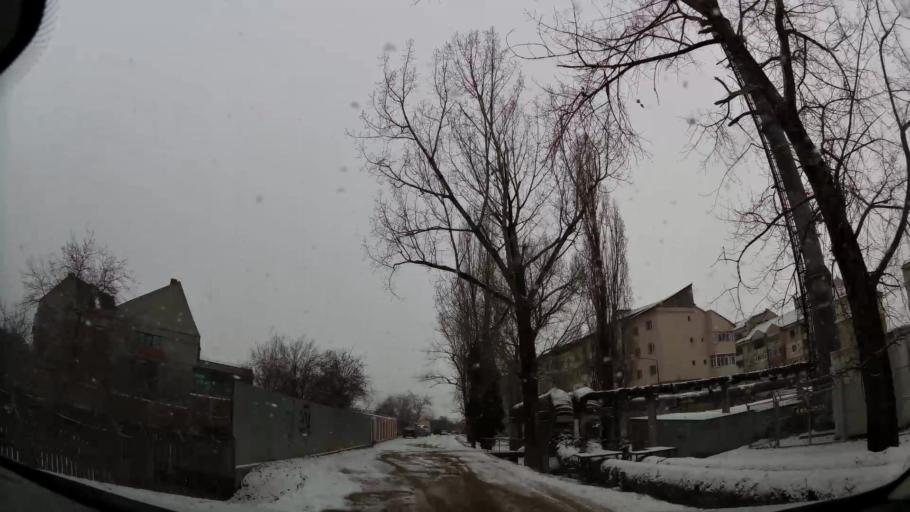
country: RO
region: Dambovita
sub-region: Municipiul Targoviste
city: Targoviste
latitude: 44.9254
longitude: 25.4505
